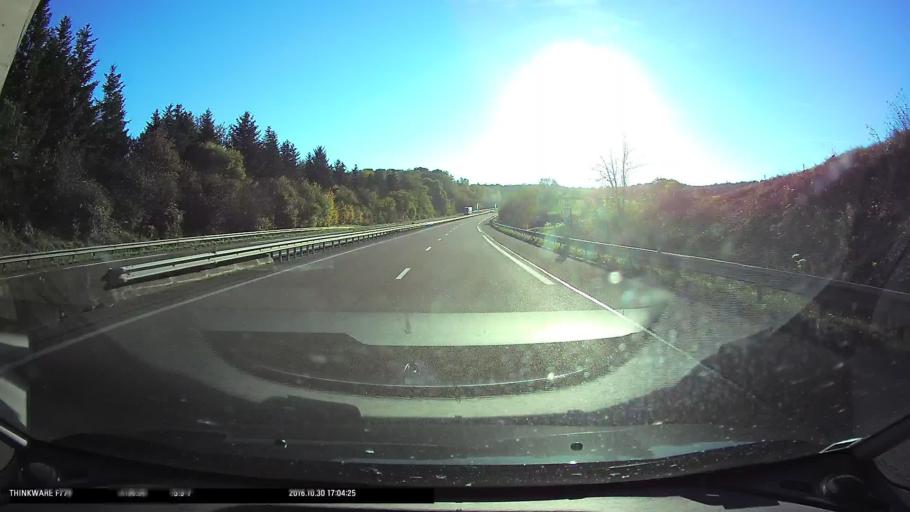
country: FR
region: Franche-Comte
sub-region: Departement du Jura
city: Orchamps
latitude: 47.1553
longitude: 5.6068
